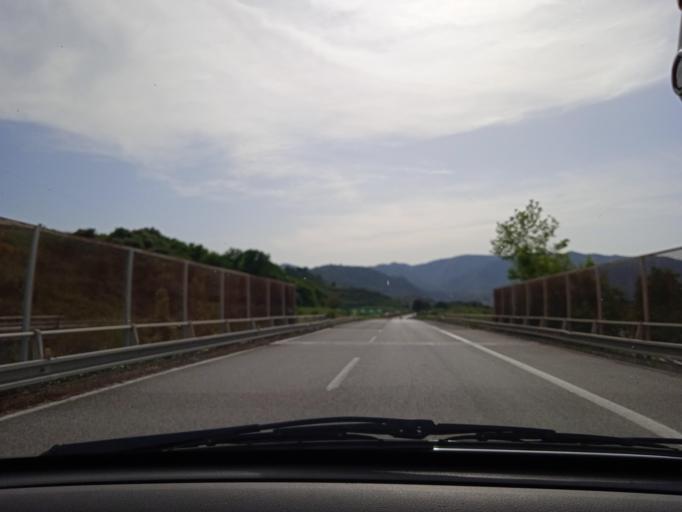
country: IT
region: Sicily
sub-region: Messina
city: Falcone
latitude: 38.1142
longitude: 15.0975
